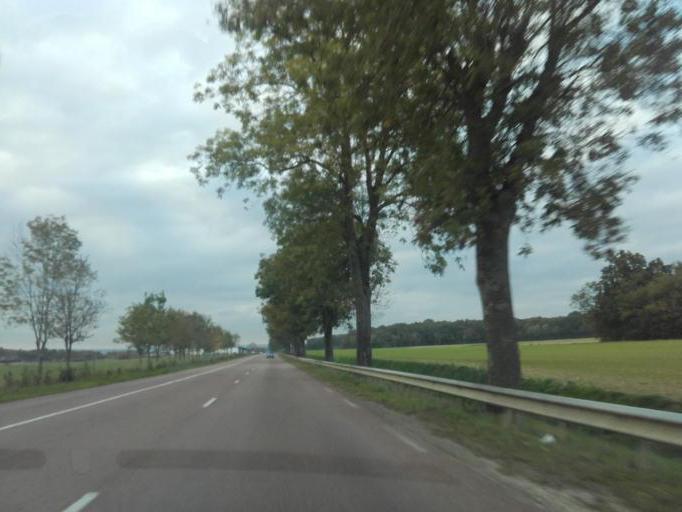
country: FR
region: Bourgogne
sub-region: Departement de Saone-et-Loire
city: Fontaines
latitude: 46.8501
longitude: 4.8071
